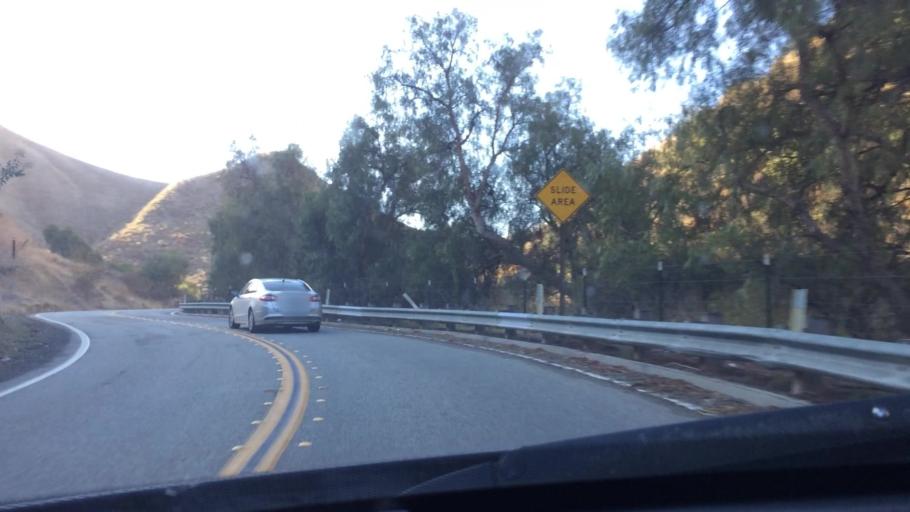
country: US
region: California
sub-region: Ventura County
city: Santa Paula
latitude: 34.3341
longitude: -118.9782
